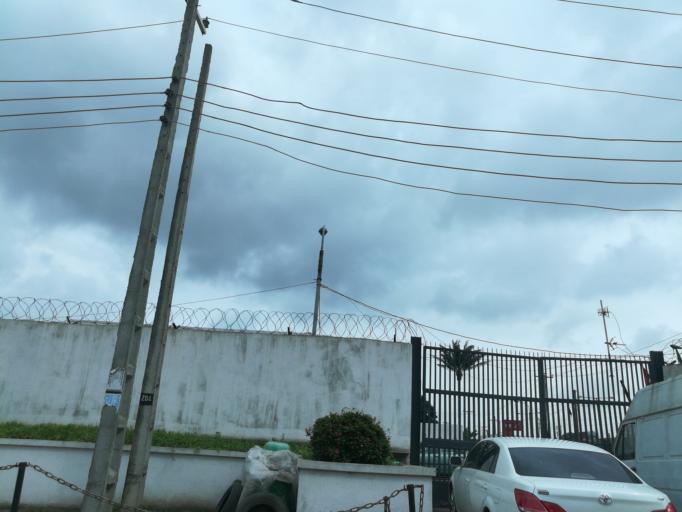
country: NG
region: Lagos
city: Ikeja
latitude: 6.6024
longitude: 3.3377
